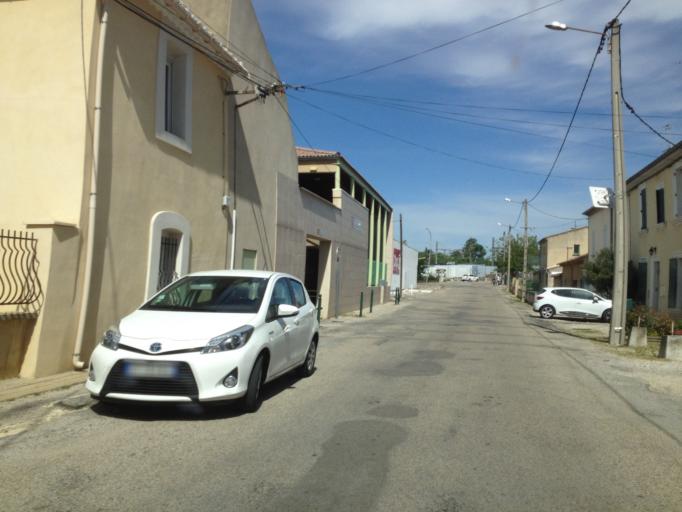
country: FR
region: Provence-Alpes-Cote d'Azur
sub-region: Departement du Vaucluse
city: Sorgues
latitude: 44.0046
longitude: 4.8738
